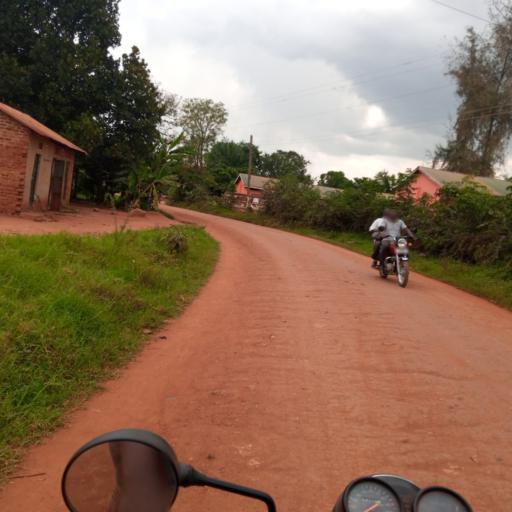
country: UG
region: Eastern Region
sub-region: Mbale District
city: Mbale
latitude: 1.1068
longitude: 34.1748
